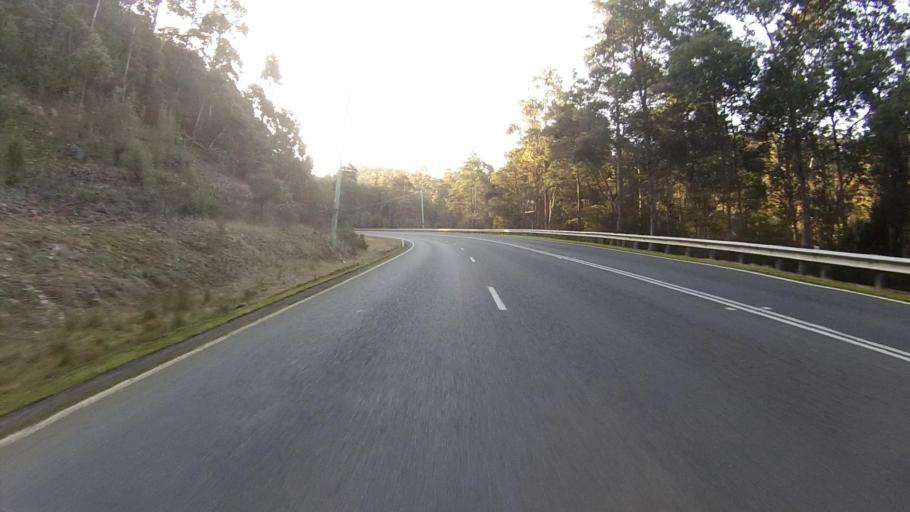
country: AU
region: Tasmania
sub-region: Sorell
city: Sorell
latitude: -42.9988
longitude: 147.9265
